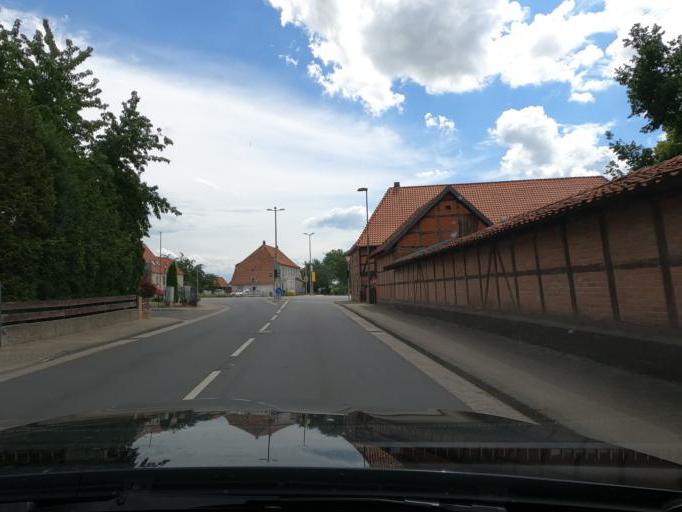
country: DE
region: Lower Saxony
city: Hohenhameln
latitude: 52.2477
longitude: 10.0263
